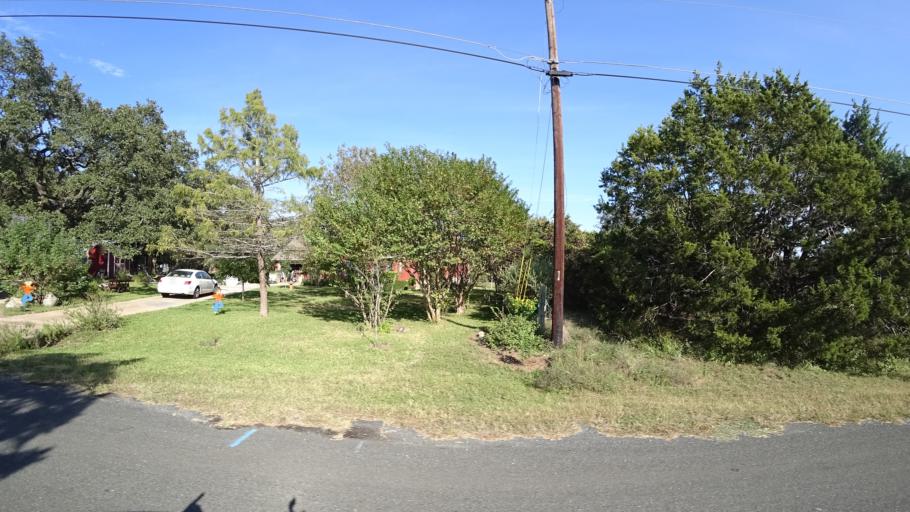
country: US
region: Texas
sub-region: Travis County
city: Bee Cave
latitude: 30.2384
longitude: -97.9355
